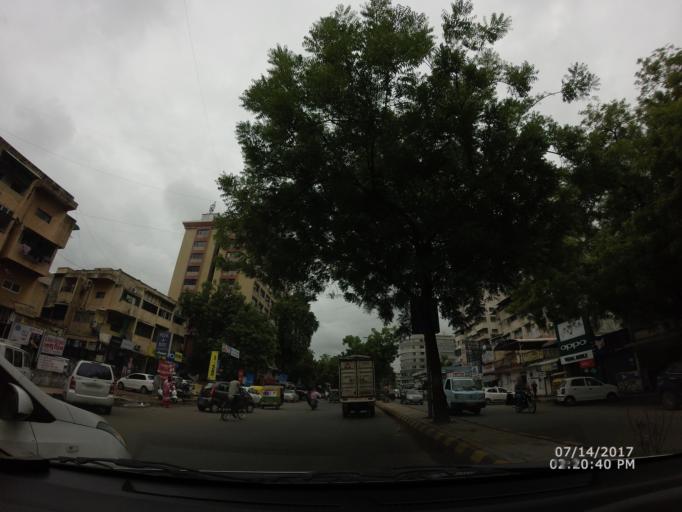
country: IN
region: Gujarat
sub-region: Ahmadabad
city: Ahmedabad
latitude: 23.0106
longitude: 72.5628
